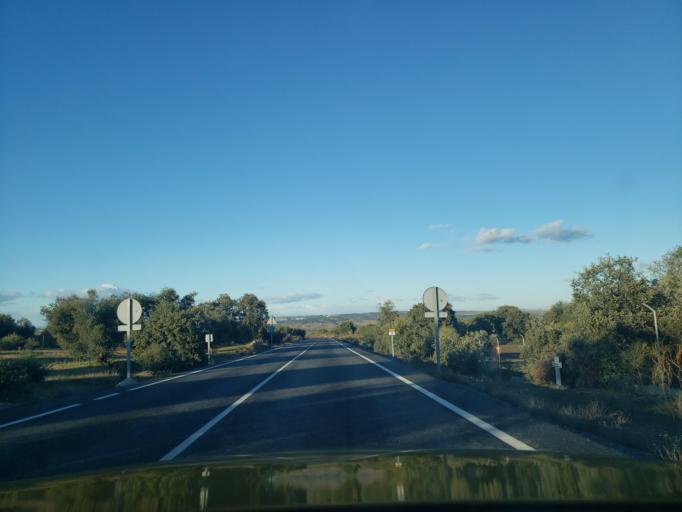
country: ES
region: Castille-La Mancha
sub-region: Province of Toledo
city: Toledo
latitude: 39.8383
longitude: -4.0192
